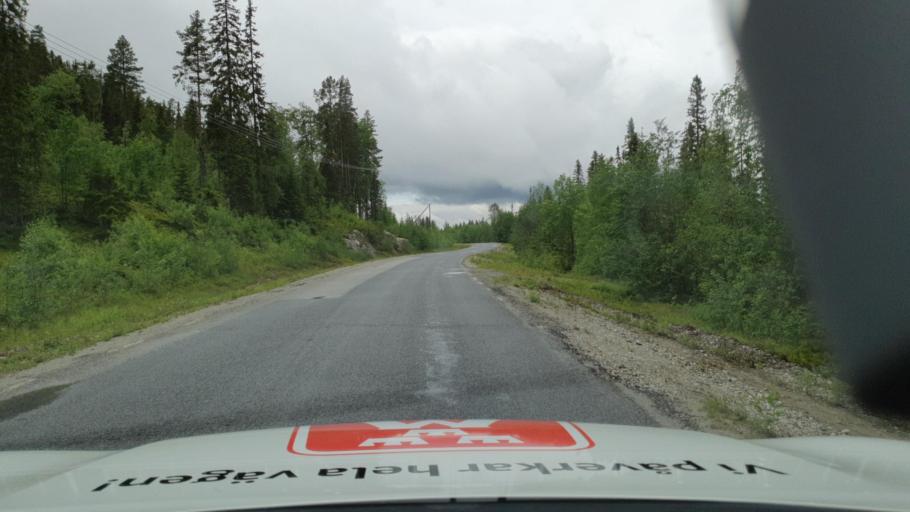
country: SE
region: Vaesterbotten
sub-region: Dorotea Kommun
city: Dorotea
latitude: 64.1766
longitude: 16.6402
